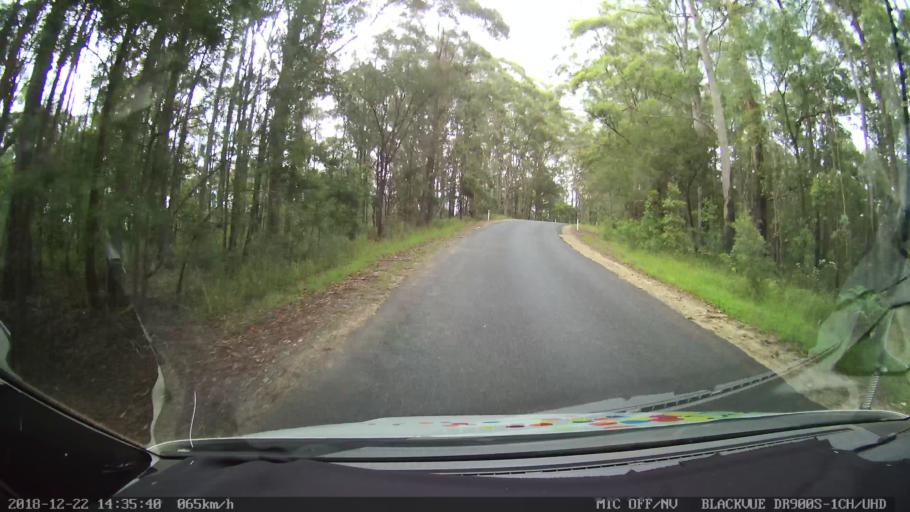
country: AU
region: New South Wales
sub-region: Bellingen
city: Dorrigo
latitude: -30.1248
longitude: 152.6124
